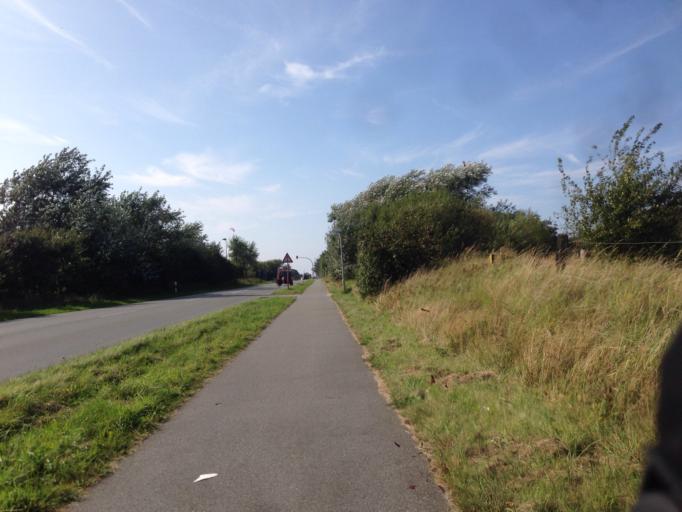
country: DE
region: Schleswig-Holstein
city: Keitum
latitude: 54.8979
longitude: 8.3551
